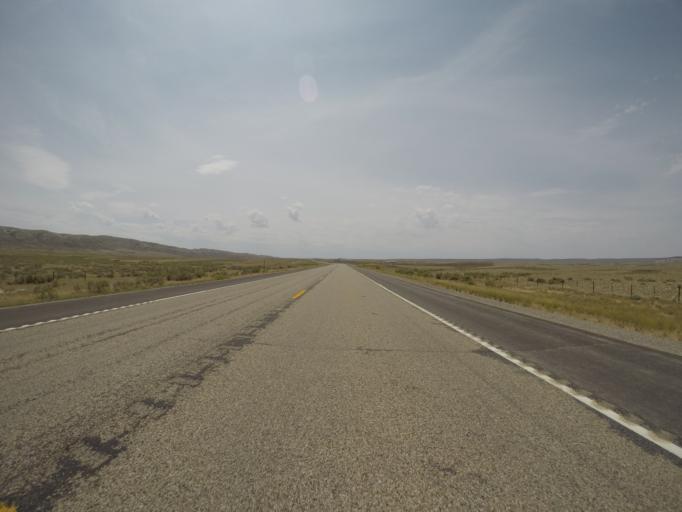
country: US
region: Wyoming
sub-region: Lincoln County
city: Kemmerer
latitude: 41.6450
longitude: -110.5716
